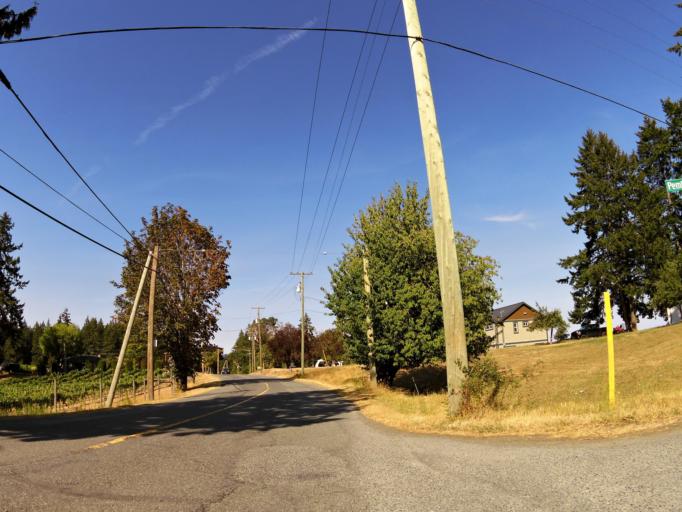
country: CA
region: British Columbia
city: North Saanich
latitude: 48.6757
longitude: -123.5514
